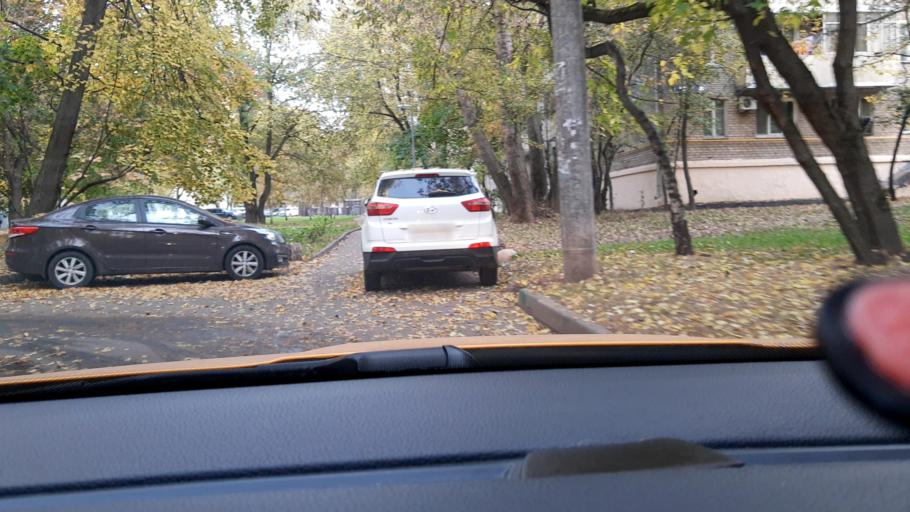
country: RU
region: Moscow
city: Businovo
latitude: 55.8774
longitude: 37.5159
